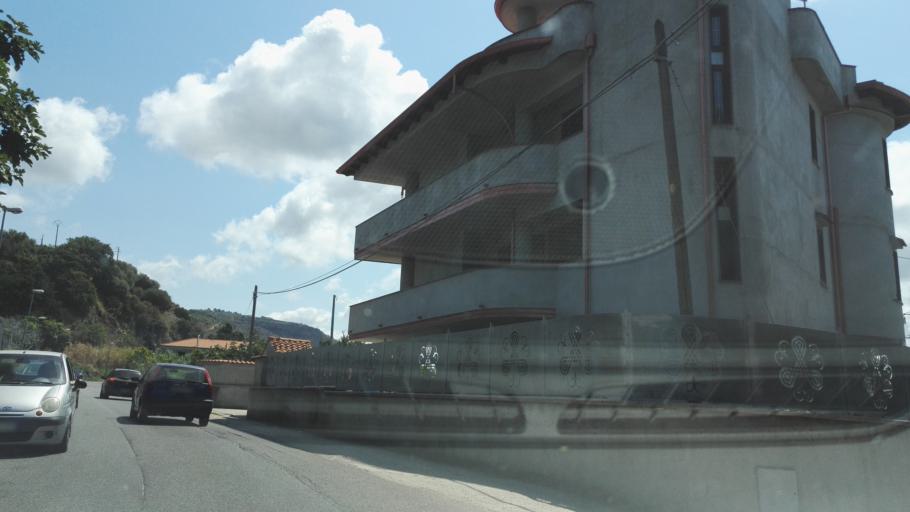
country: IT
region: Calabria
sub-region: Provincia di Vibo-Valentia
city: Nicotera
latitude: 38.5464
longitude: 15.9404
